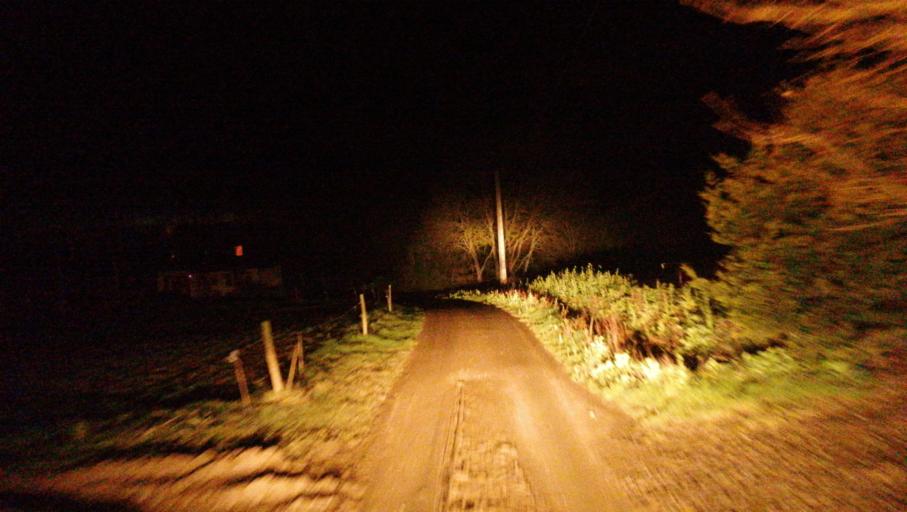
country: FR
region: Brittany
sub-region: Departement des Cotes-d'Armor
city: Lanvollon
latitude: 48.6397
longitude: -3.0094
